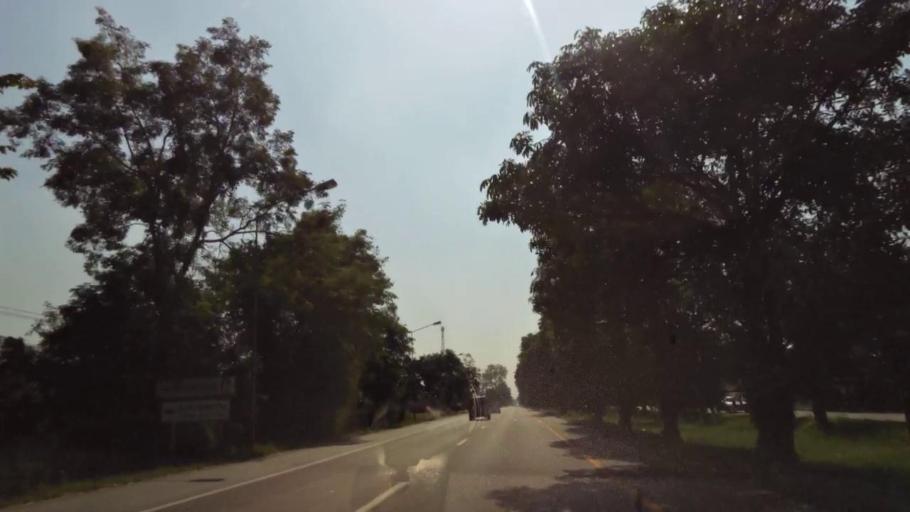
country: TH
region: Phichit
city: Wachira Barami
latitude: 16.6362
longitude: 100.1496
